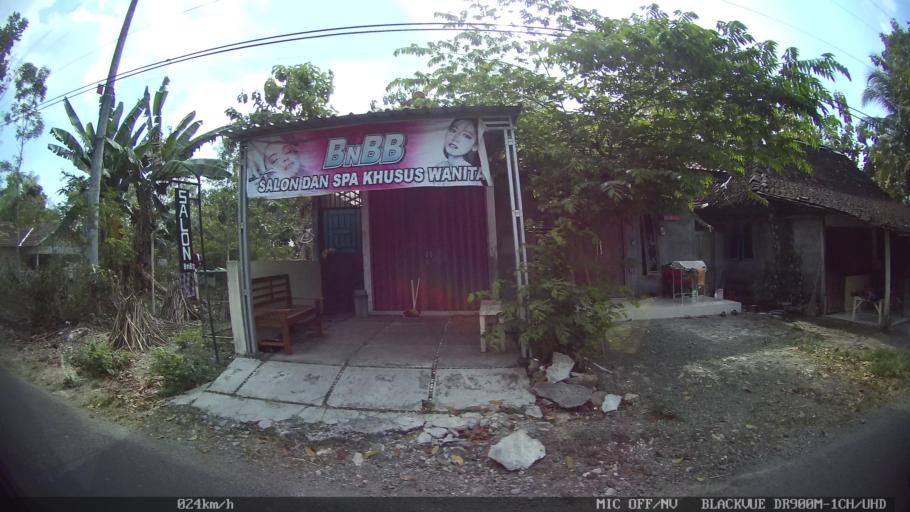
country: ID
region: Daerah Istimewa Yogyakarta
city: Kasihan
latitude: -7.8544
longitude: 110.3108
